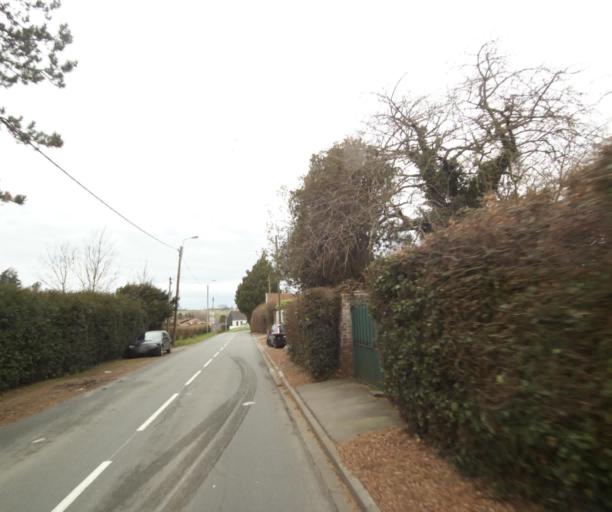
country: FR
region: Nord-Pas-de-Calais
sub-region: Departement du Nord
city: Sebourg
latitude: 50.3334
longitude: 3.6550
